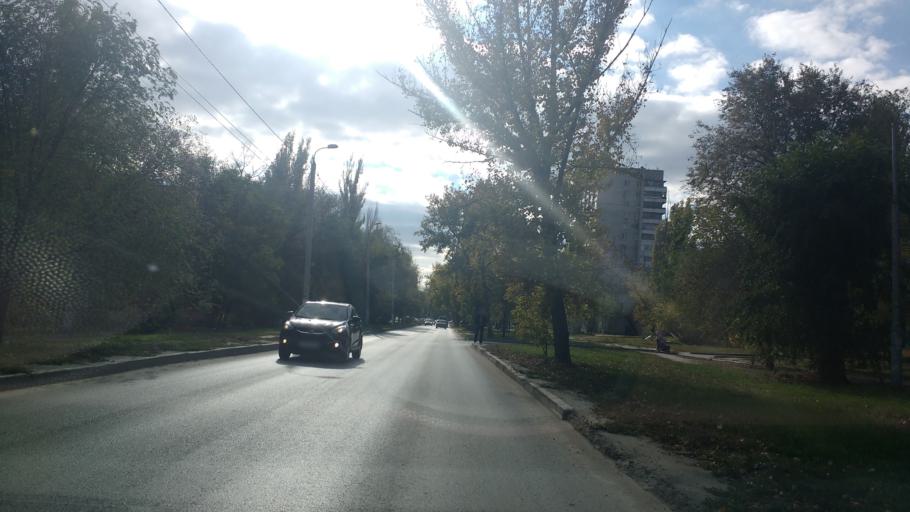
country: RU
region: Volgograd
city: Vodstroy
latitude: 48.7753
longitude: 44.5625
